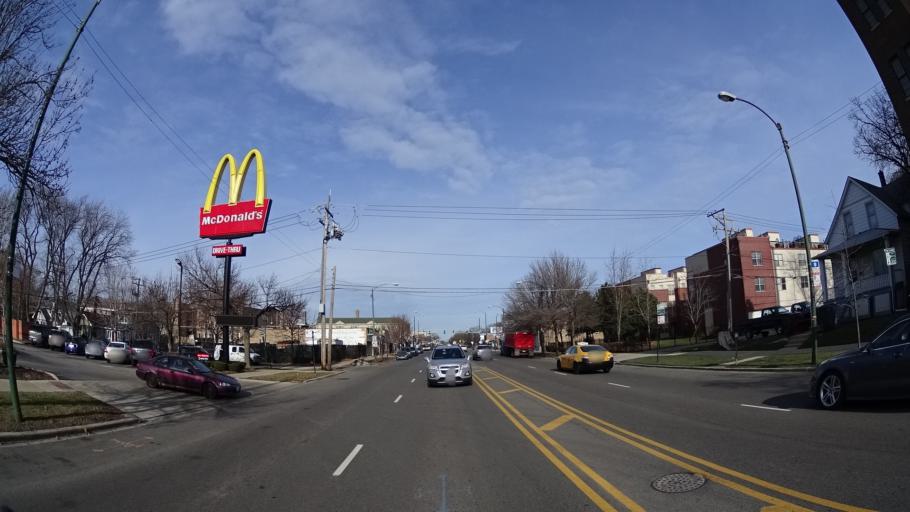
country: US
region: Illinois
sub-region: Cook County
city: Evanston
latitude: 42.0075
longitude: -87.6901
